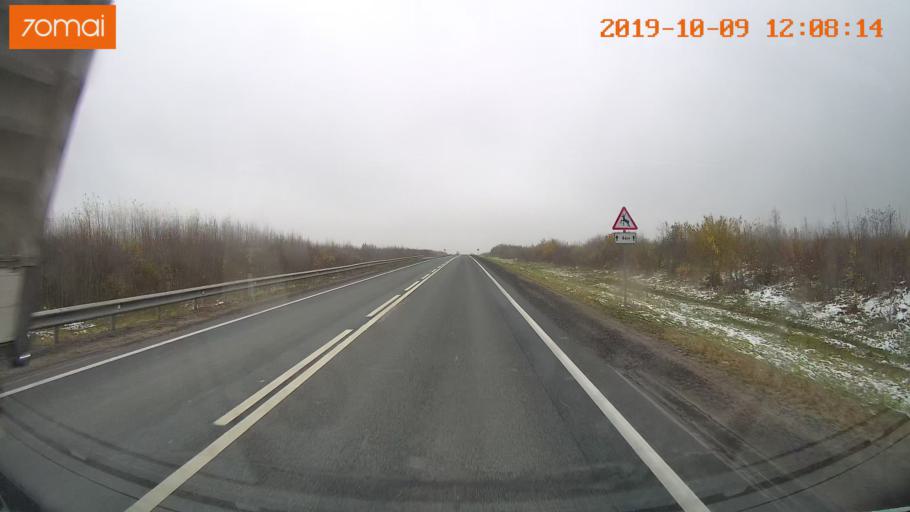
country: RU
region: Jaroslavl
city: Prechistoye
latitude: 58.5891
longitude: 40.3463
